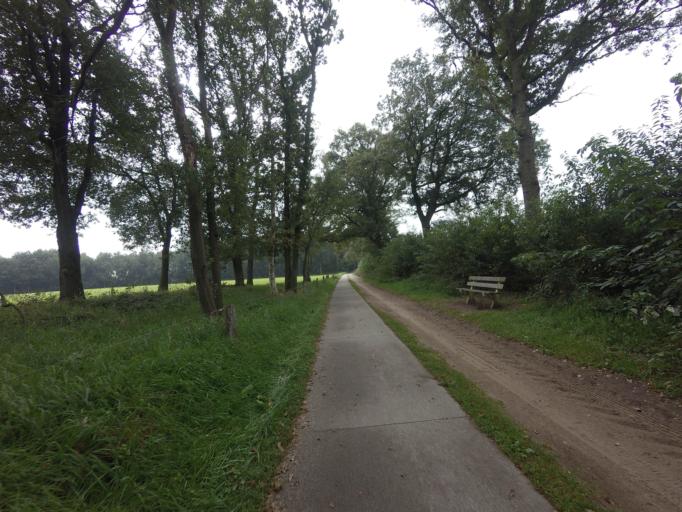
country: DE
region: Lower Saxony
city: Getelo
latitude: 52.4482
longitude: 6.8714
